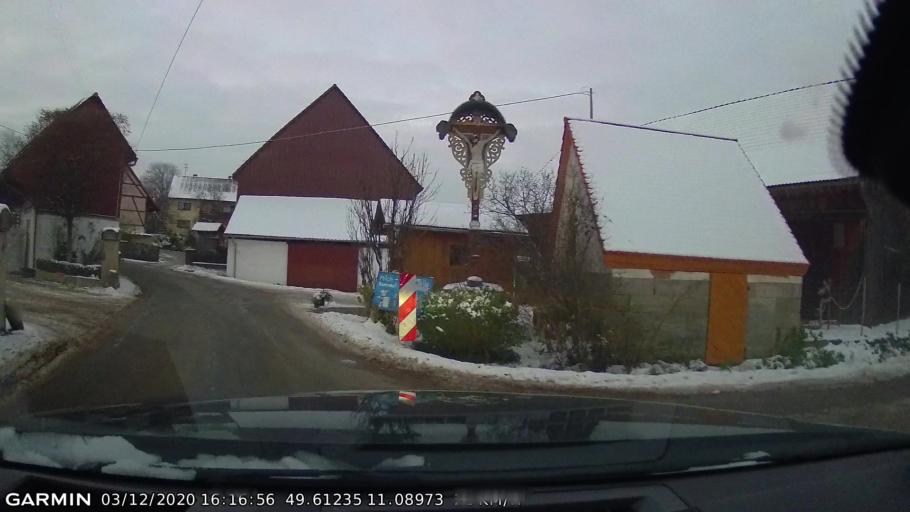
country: DE
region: Bavaria
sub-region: Regierungsbezirk Mittelfranken
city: Uttenreuth
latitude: 49.6123
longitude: 11.0897
